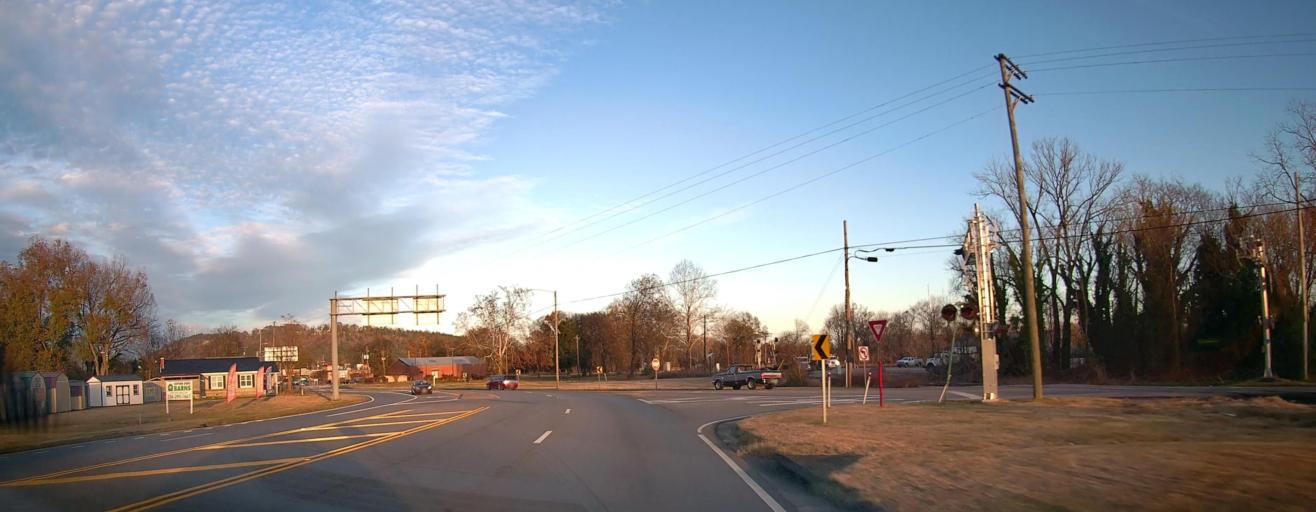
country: US
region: Alabama
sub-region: Etowah County
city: Attalla
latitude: 34.0185
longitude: -86.0937
